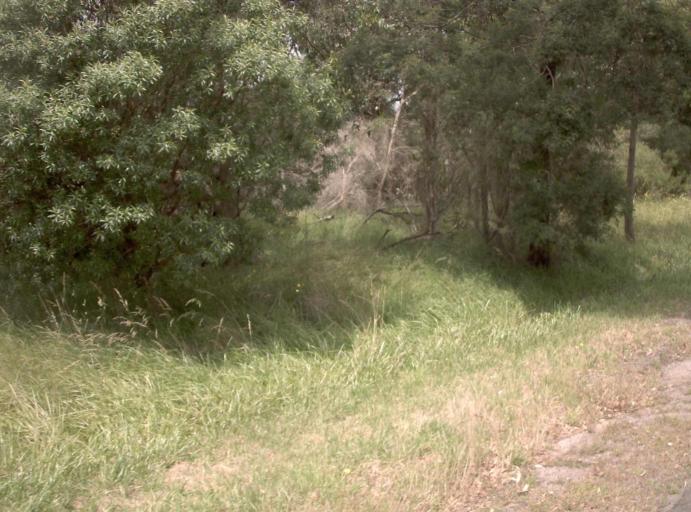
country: AU
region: Victoria
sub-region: Latrobe
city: Traralgon
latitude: -38.4823
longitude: 146.7151
